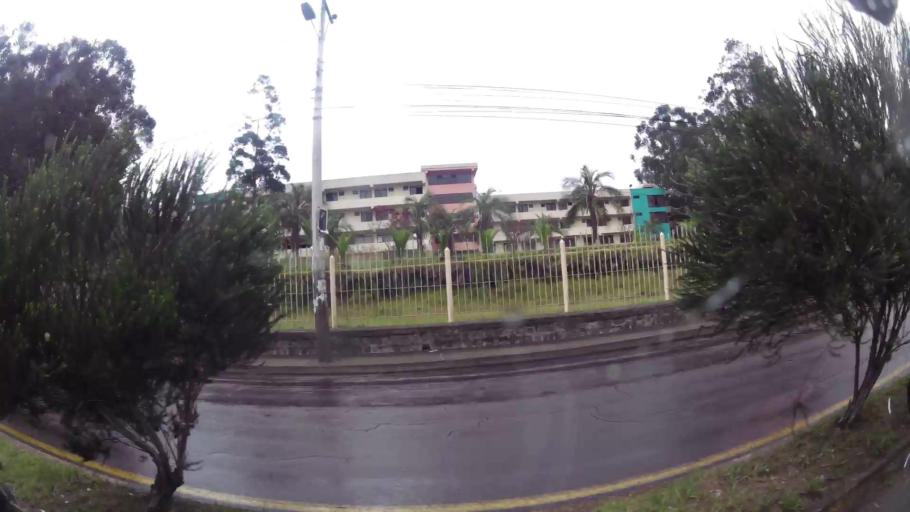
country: EC
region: Pichincha
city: Sangolqui
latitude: -0.3167
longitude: -78.4422
